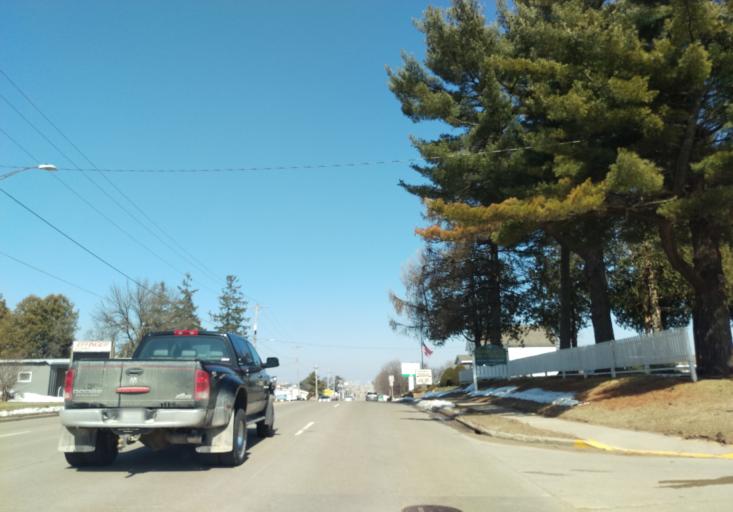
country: US
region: Wisconsin
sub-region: Vernon County
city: Viroqua
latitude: 43.5635
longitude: -90.8889
